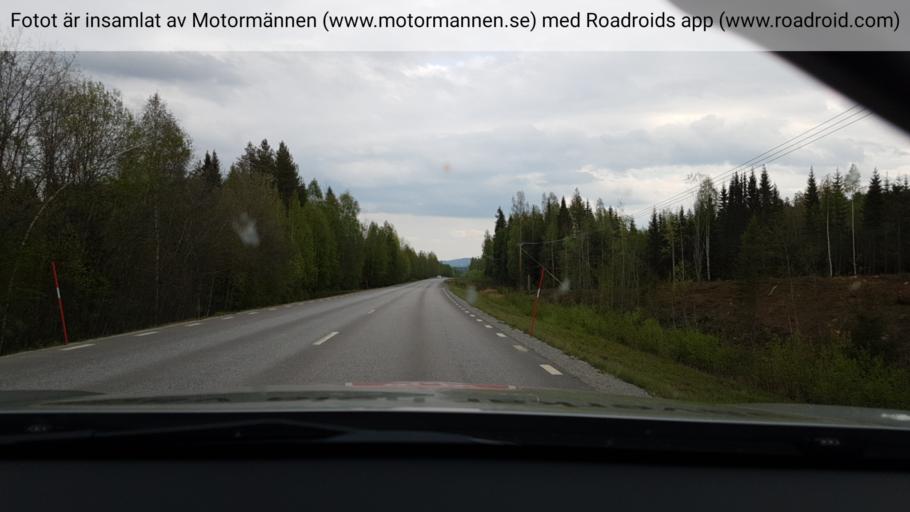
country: SE
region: Vaesterbotten
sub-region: Vannas Kommun
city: Vaennaes
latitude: 63.9251
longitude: 19.5903
